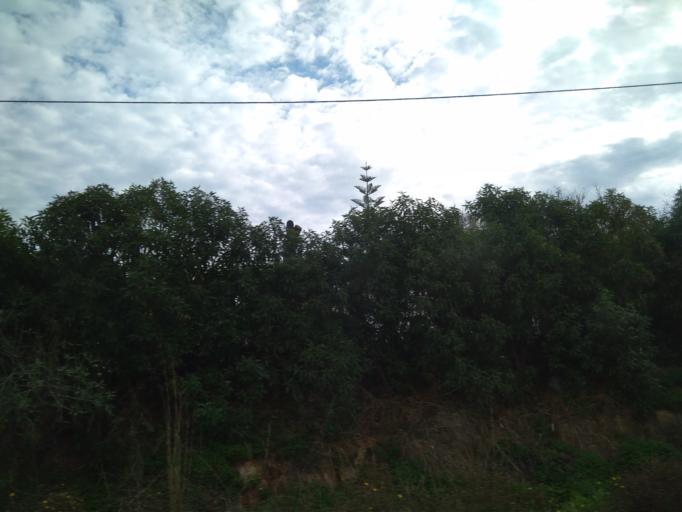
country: PT
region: Faro
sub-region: Olhao
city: Laranjeiro
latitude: 37.0458
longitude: -7.7971
